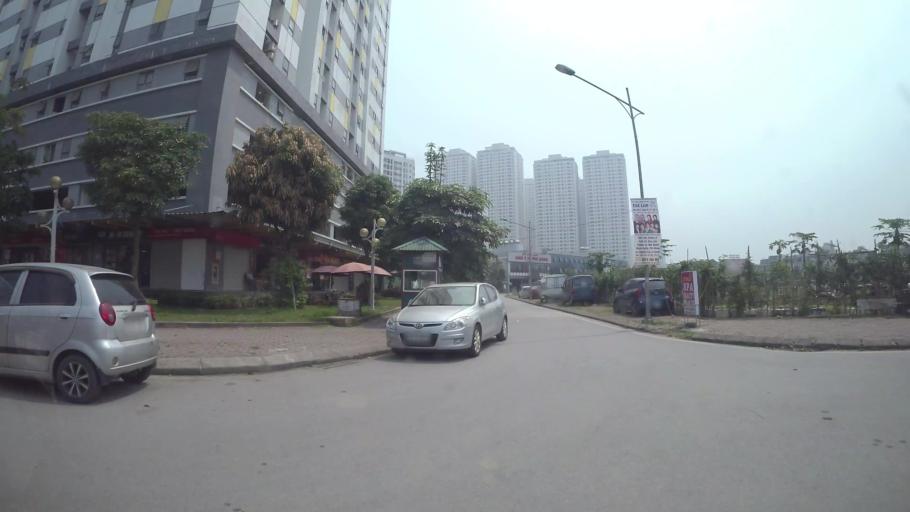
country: VN
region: Ha Noi
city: Van Dien
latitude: 20.9626
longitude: 105.8226
